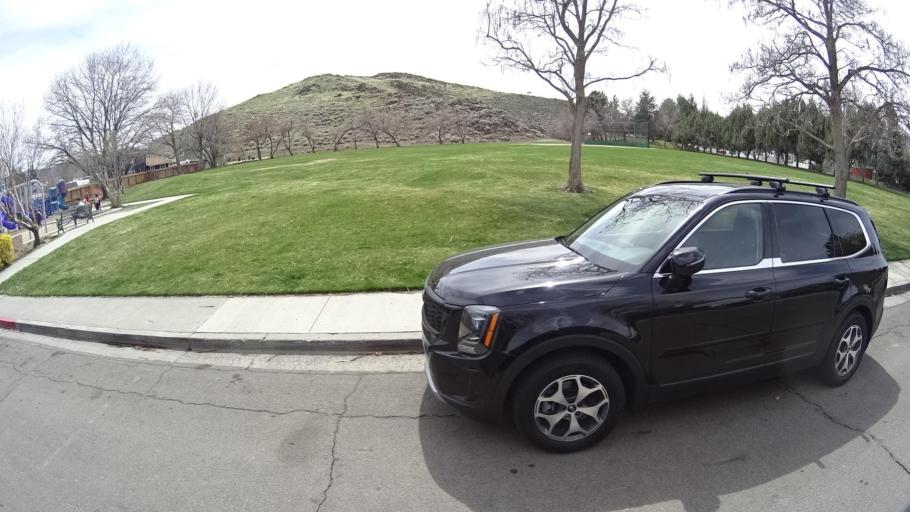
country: US
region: Nevada
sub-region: Washoe County
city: Sparks
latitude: 39.4573
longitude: -119.7673
